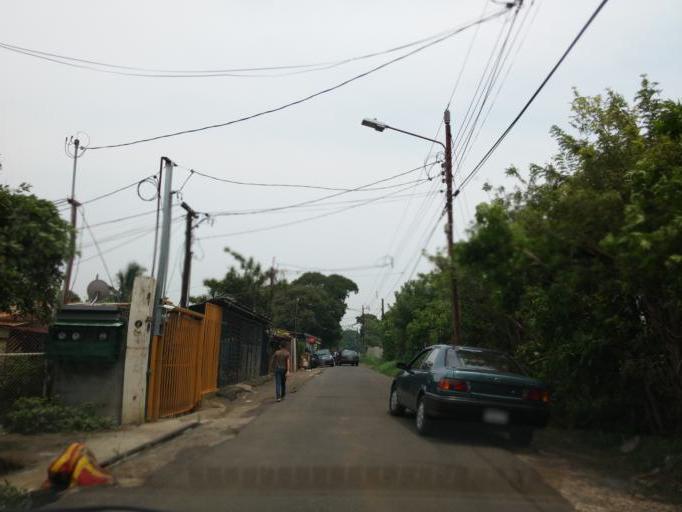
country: CR
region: Heredia
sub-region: Canton de Belen
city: San Antonio
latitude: 9.9929
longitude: -84.2014
